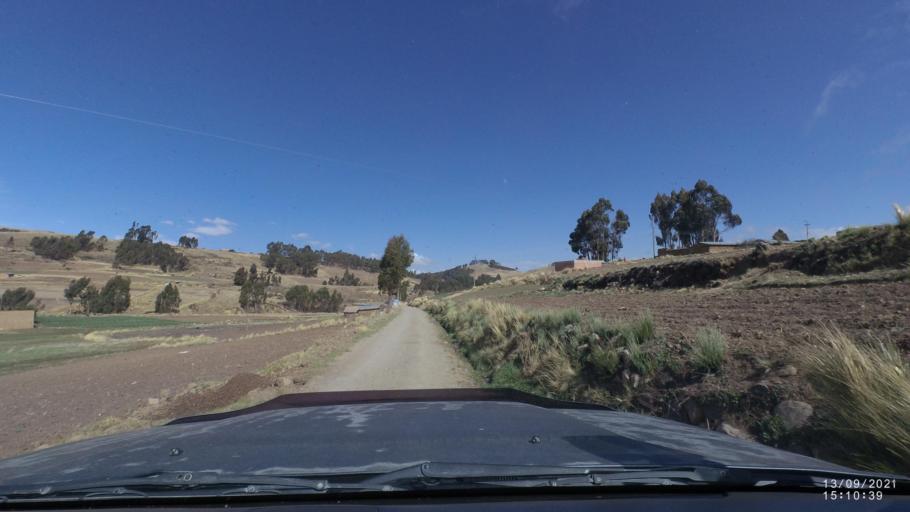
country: BO
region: Cochabamba
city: Colomi
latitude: -17.3559
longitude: -65.8046
